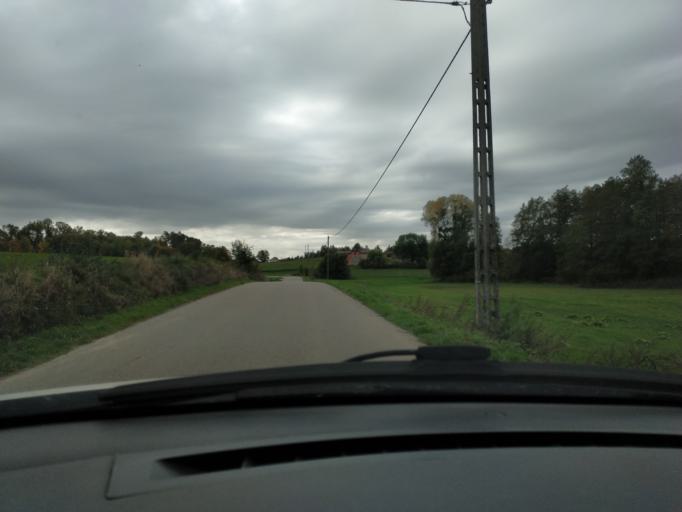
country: PL
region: Warmian-Masurian Voivodeship
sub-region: Powiat nowomiejski
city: Biskupiec
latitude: 53.4575
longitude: 19.3166
